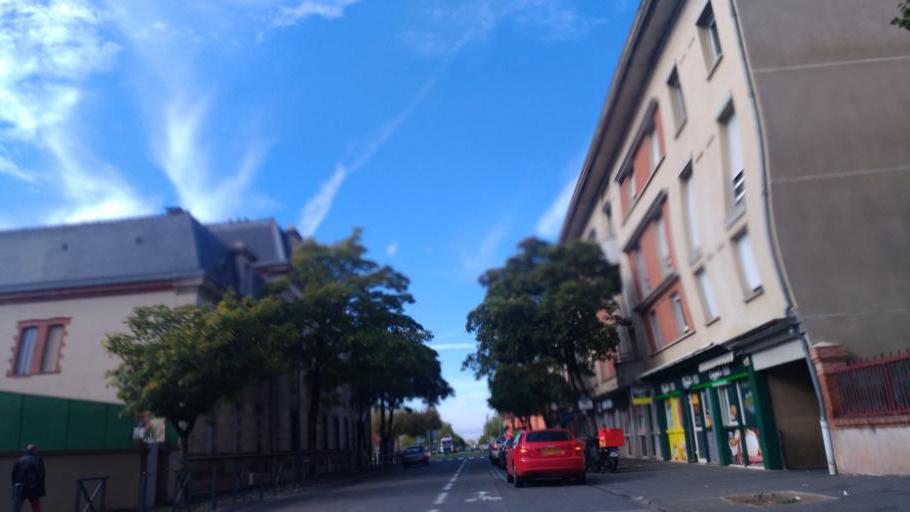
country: FR
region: Midi-Pyrenees
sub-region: Departement du Tarn
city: Albi
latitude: 43.9200
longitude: 2.1407
